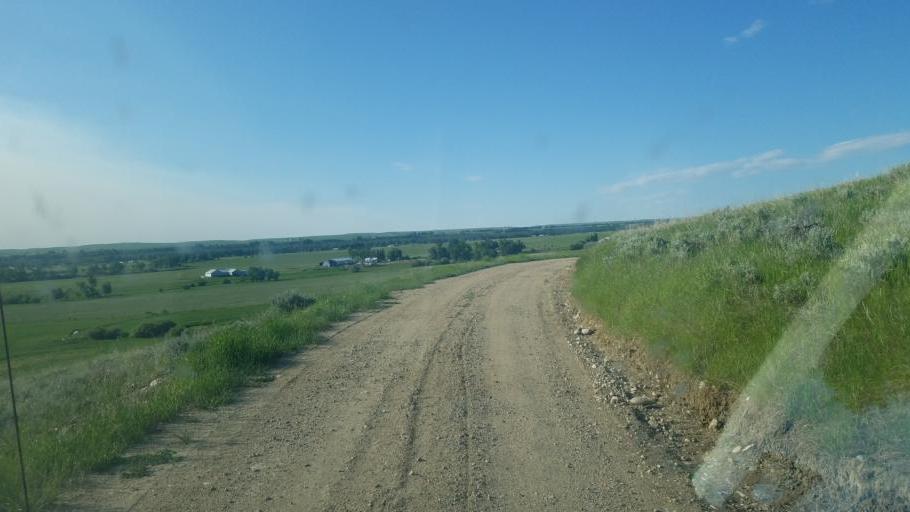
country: US
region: Montana
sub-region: Carbon County
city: Red Lodge
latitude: 45.3696
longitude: -109.1899
